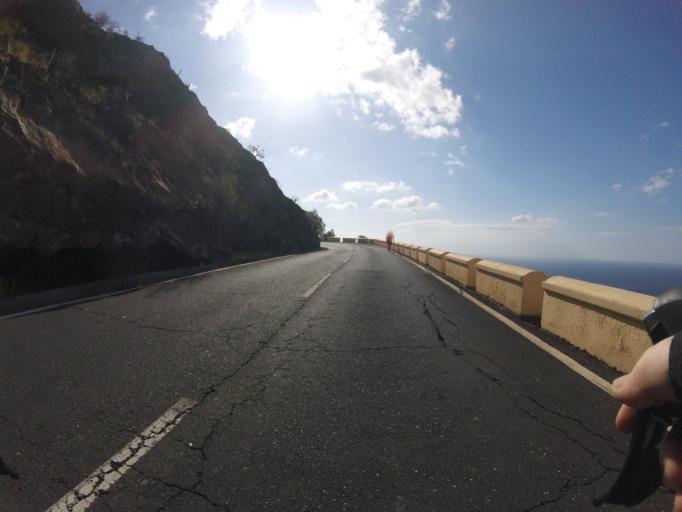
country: ES
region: Canary Islands
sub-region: Provincia de Santa Cruz de Tenerife
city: Candelaria
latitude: 28.4075
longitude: -16.3405
